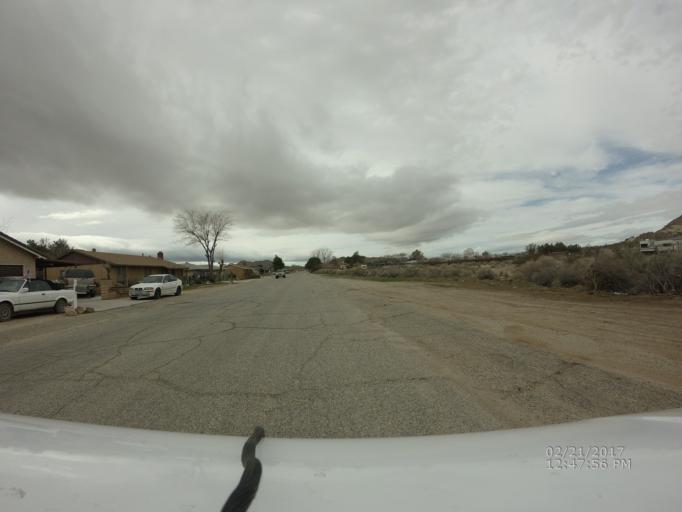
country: US
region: California
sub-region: Los Angeles County
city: Lake Los Angeles
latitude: 34.6398
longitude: -117.8473
